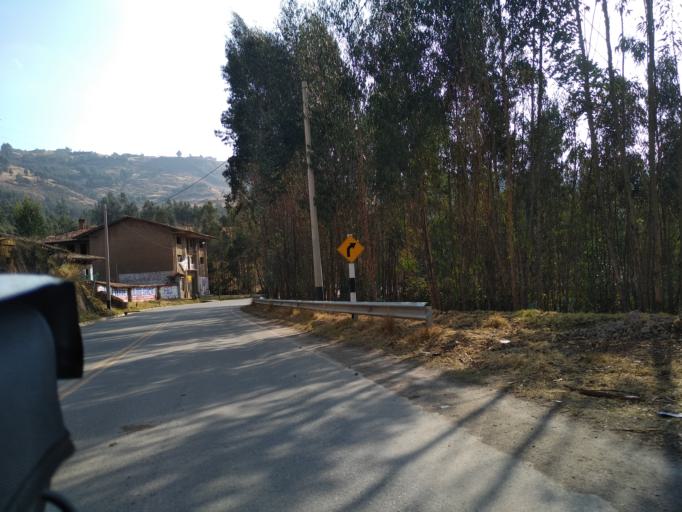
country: PE
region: La Libertad
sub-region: Provincia de Otuzco
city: Agallpampa
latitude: -7.9967
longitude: -78.5196
